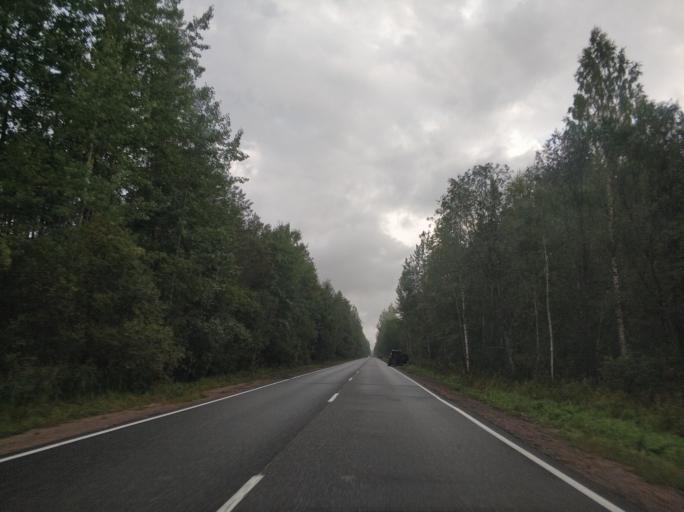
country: RU
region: Leningrad
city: Borisova Griva
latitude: 60.1447
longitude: 30.9458
